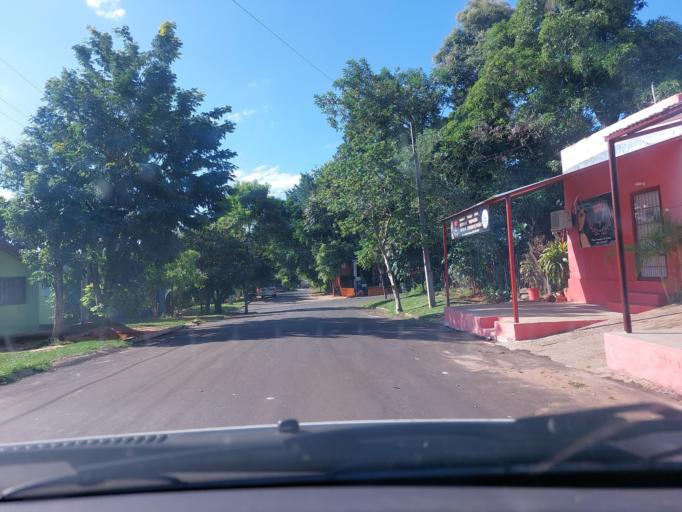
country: PY
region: San Pedro
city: Guayaybi
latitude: -24.6590
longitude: -56.4446
